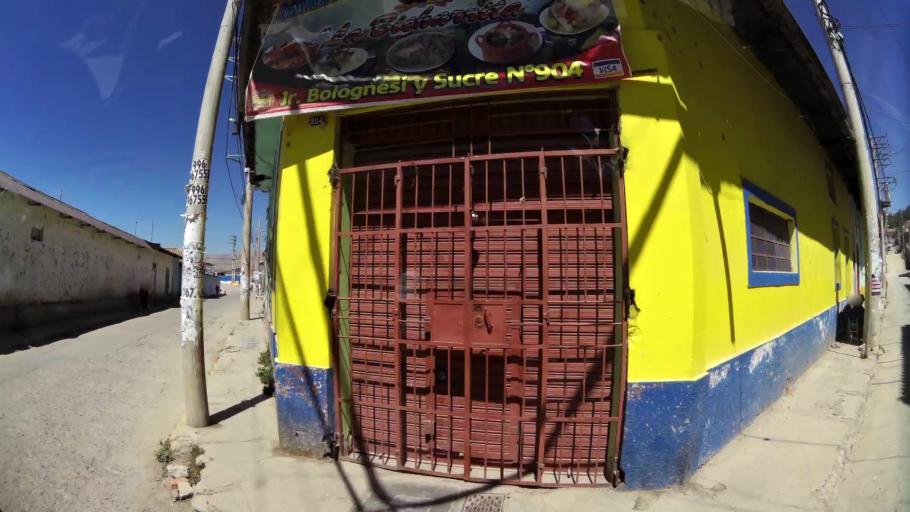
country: PE
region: Junin
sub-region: Provincia de Jauja
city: Jauja
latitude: -11.7763
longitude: -75.5010
